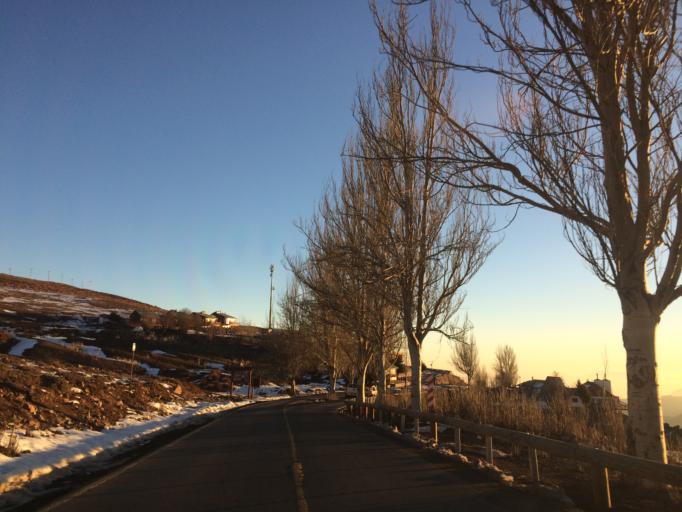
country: CL
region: Santiago Metropolitan
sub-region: Provincia de Santiago
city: Villa Presidente Frei, Nunoa, Santiago, Chile
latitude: -33.3440
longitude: -70.2984
